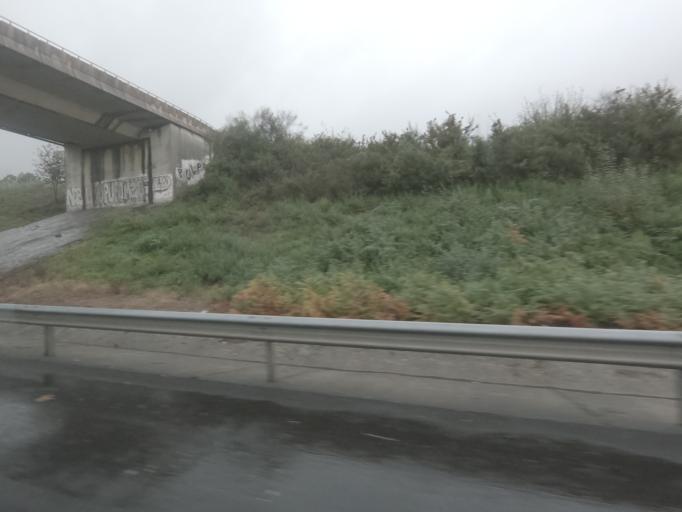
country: ES
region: Galicia
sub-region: Provincia de Pontevedra
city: Redondela
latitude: 42.2345
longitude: -8.6524
